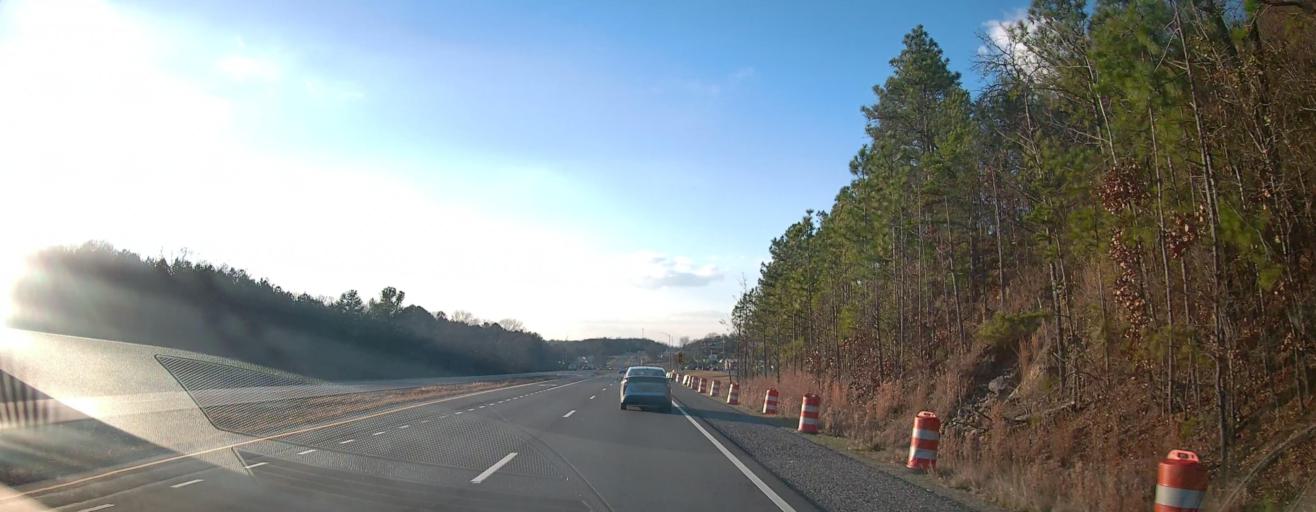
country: US
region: Alabama
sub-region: Calhoun County
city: Saks
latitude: 33.7150
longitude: -85.8534
